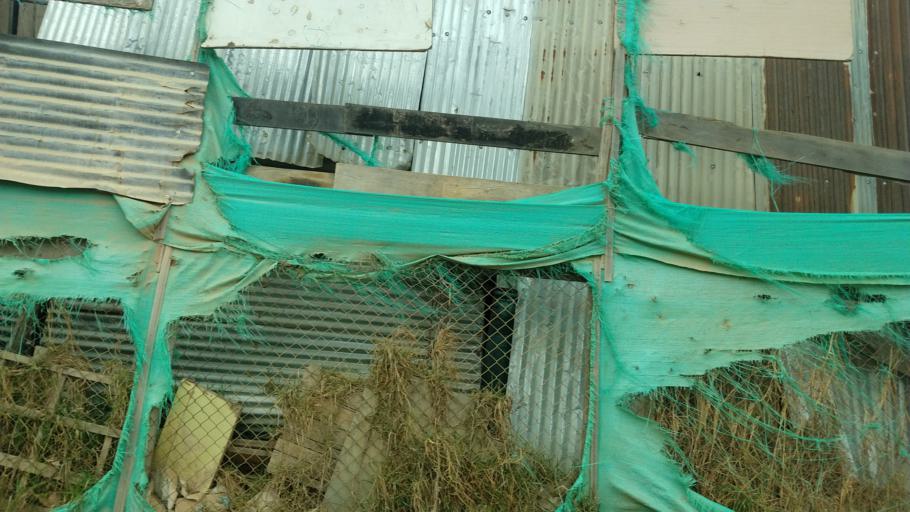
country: CO
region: Cundinamarca
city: Soacha
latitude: 4.5633
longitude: -74.1894
